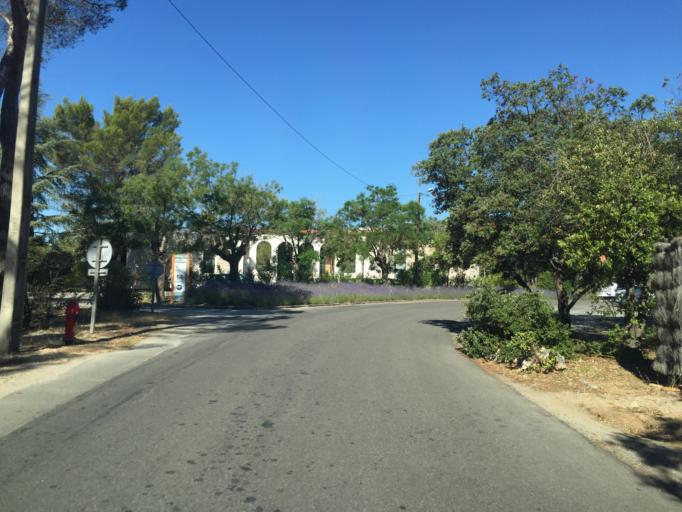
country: FR
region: Provence-Alpes-Cote d'Azur
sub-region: Departement des Bouches-du-Rhone
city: Ventabren
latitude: 43.4898
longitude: 5.3330
